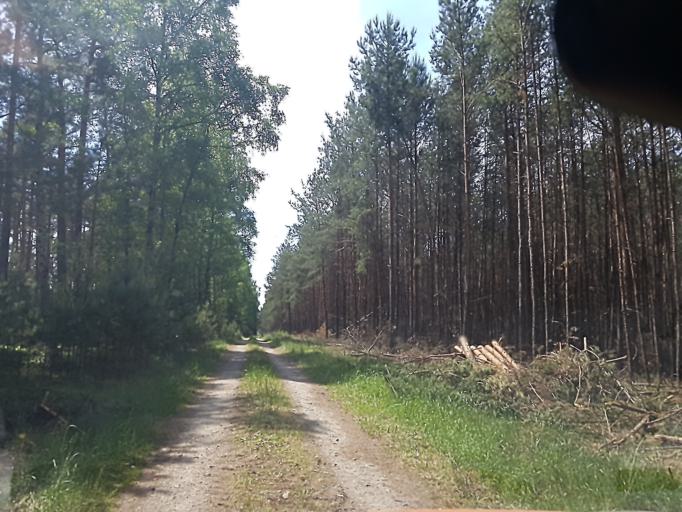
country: DE
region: Brandenburg
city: Gorzke
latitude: 52.1098
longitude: 12.2980
